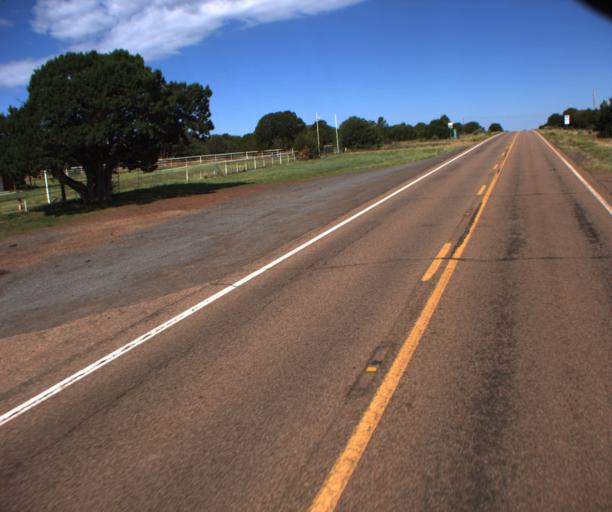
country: US
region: Arizona
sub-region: Navajo County
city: White Mountain Lake
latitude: 34.2792
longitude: -109.8006
